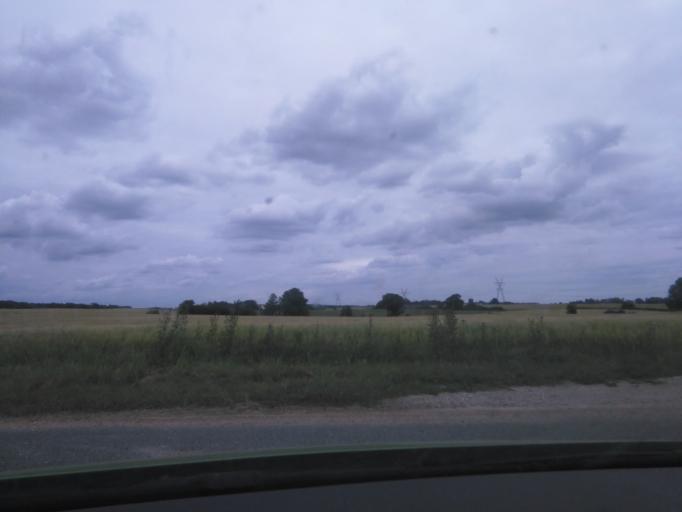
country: DK
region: Central Jutland
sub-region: Arhus Kommune
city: Solbjerg
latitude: 55.9918
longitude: 10.0918
